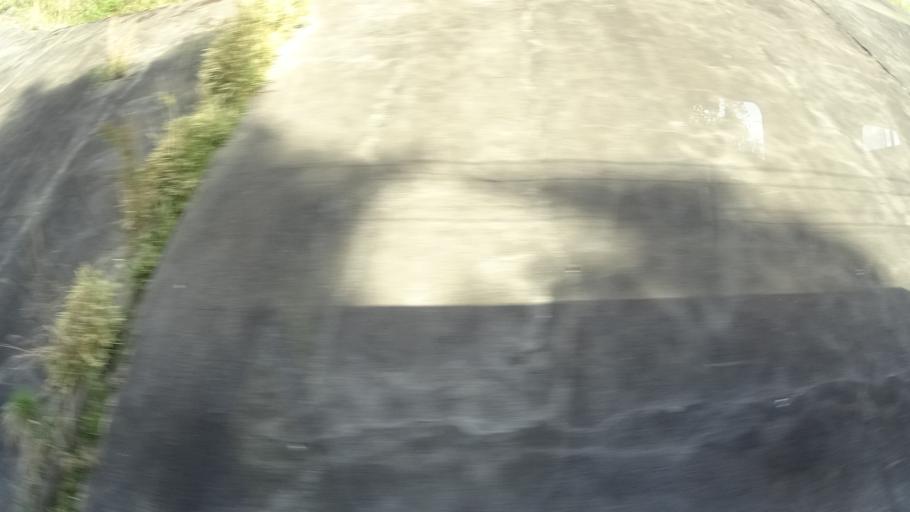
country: JP
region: Fukushima
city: Namie
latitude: 37.5485
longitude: 140.9936
